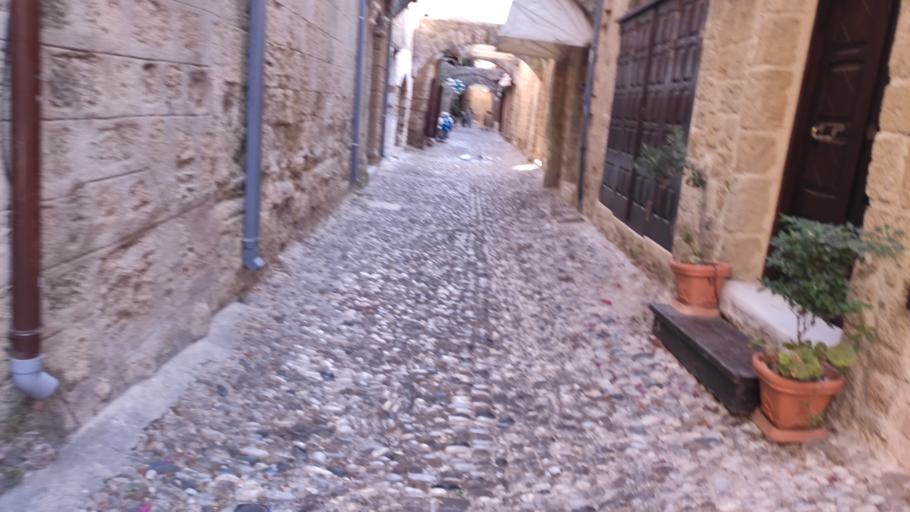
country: GR
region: South Aegean
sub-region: Nomos Dodekanisou
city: Rodos
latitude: 36.4419
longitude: 28.2258
